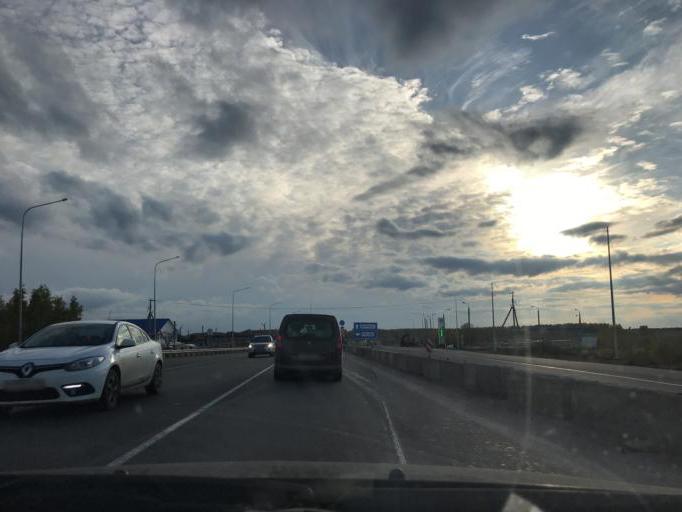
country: RU
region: Kaluga
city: Kurovskoye
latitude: 54.5308
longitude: 35.9906
